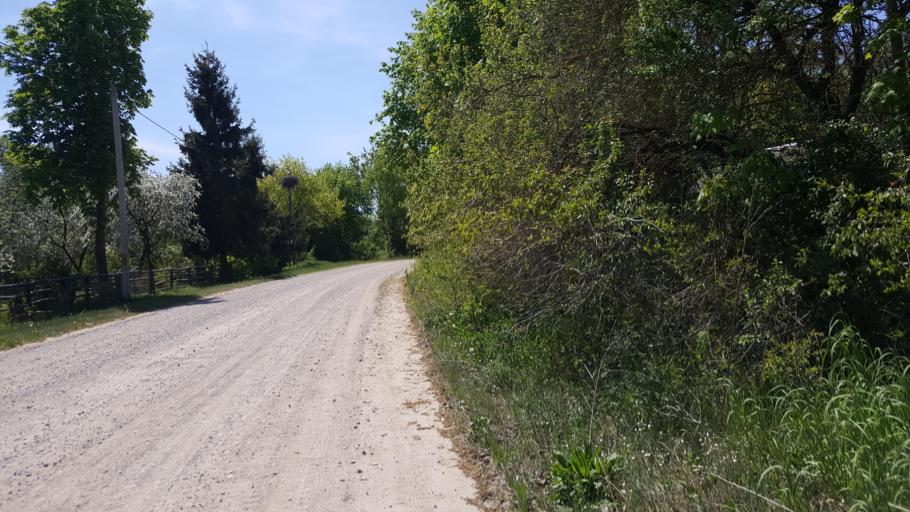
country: BY
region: Brest
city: Zhabinka
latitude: 52.3553
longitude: 24.1548
